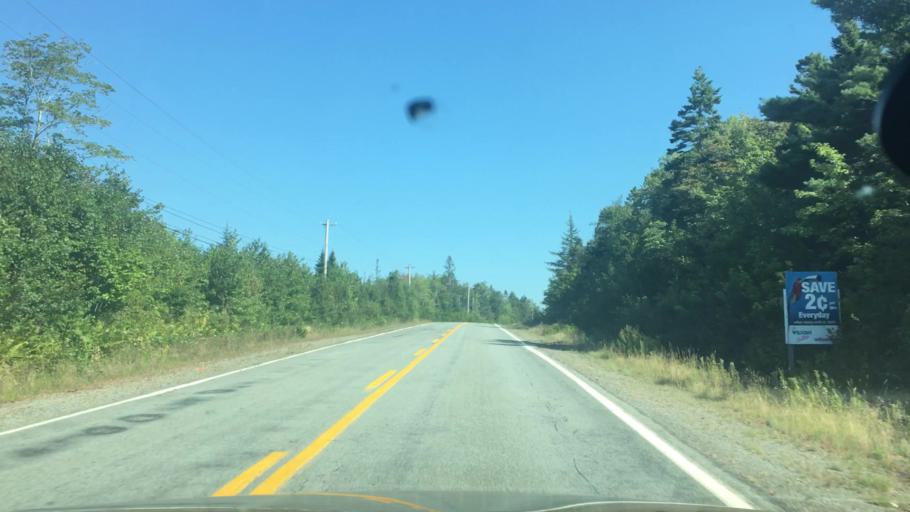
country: CA
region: Nova Scotia
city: New Glasgow
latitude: 44.9072
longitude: -62.5558
